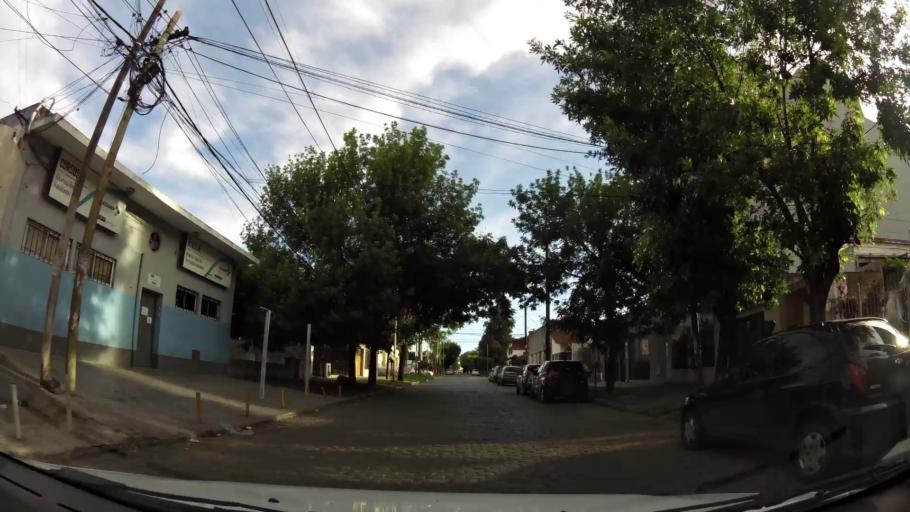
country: AR
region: Buenos Aires
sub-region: Partido de Moron
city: Moron
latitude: -34.6577
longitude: -58.6187
